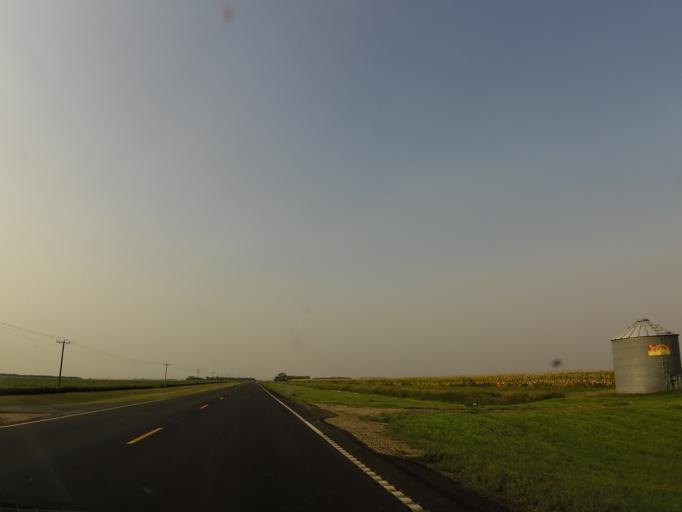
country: US
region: North Dakota
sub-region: Traill County
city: Mayville
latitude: 47.3761
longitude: -97.3265
